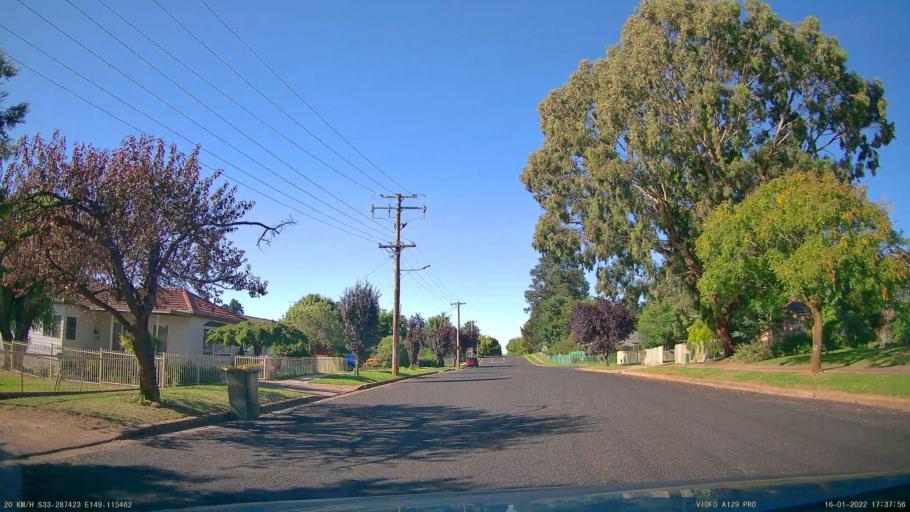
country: AU
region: New South Wales
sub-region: Orange Municipality
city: Orange
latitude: -33.2873
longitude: 149.1155
